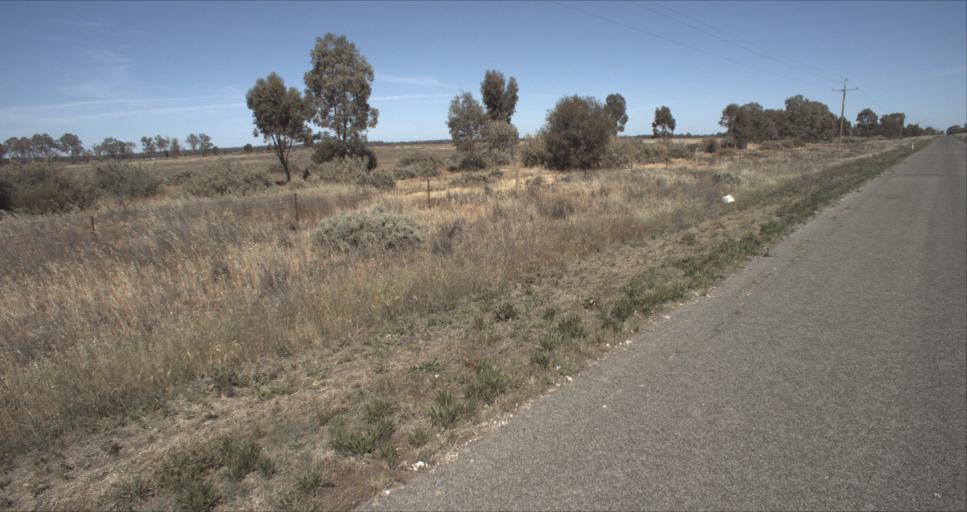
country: AU
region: New South Wales
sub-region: Leeton
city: Leeton
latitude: -34.5818
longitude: 146.2960
